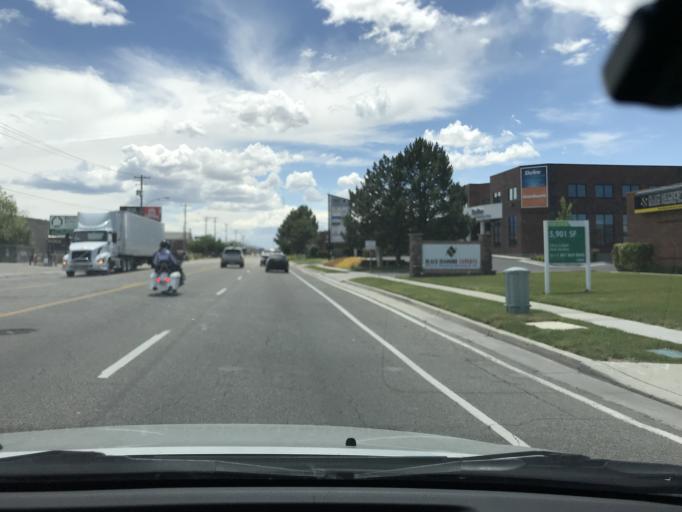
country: US
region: Utah
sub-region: Salt Lake County
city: South Salt Lake
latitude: 40.7094
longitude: -111.8998
